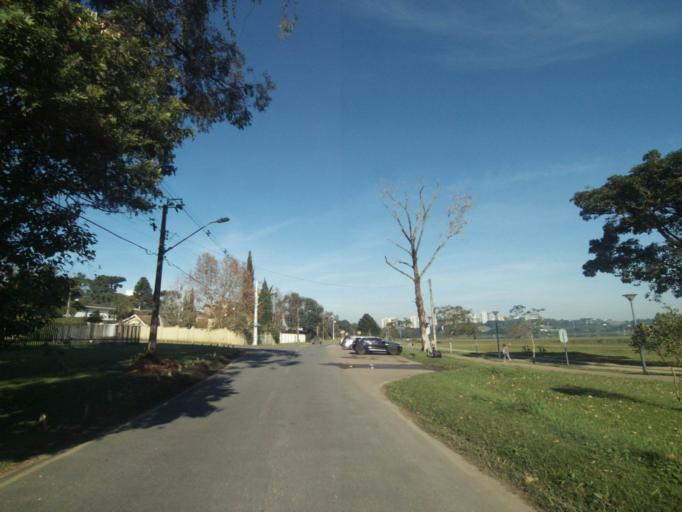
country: BR
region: Parana
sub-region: Curitiba
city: Curitiba
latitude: -25.4286
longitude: -49.3056
